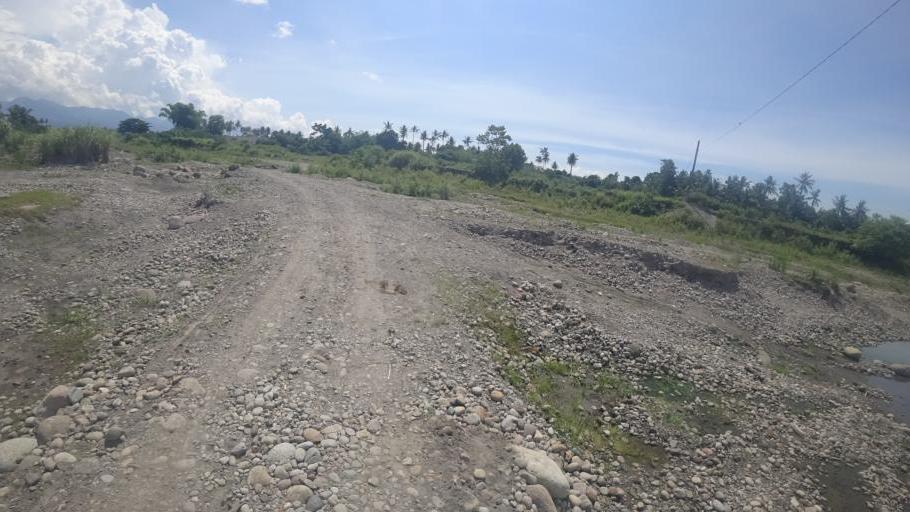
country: PH
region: Eastern Visayas
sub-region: Province of Leyte
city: Jaro
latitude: 11.1996
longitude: 124.8091
